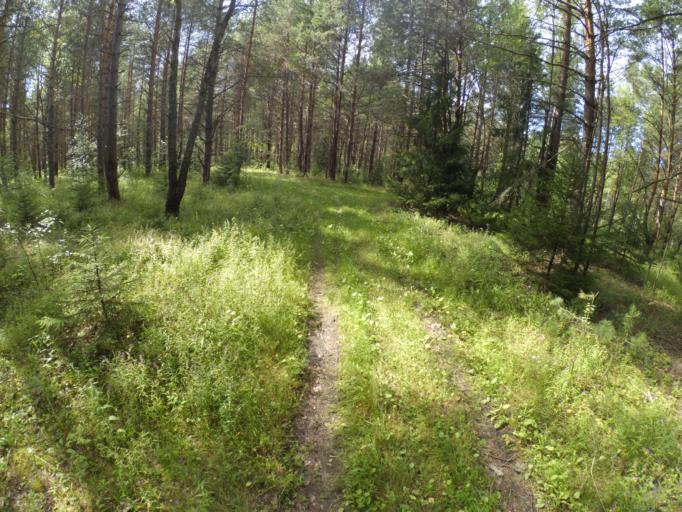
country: RU
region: Moskovskaya
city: Fosforitnyy
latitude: 55.3328
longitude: 38.9327
